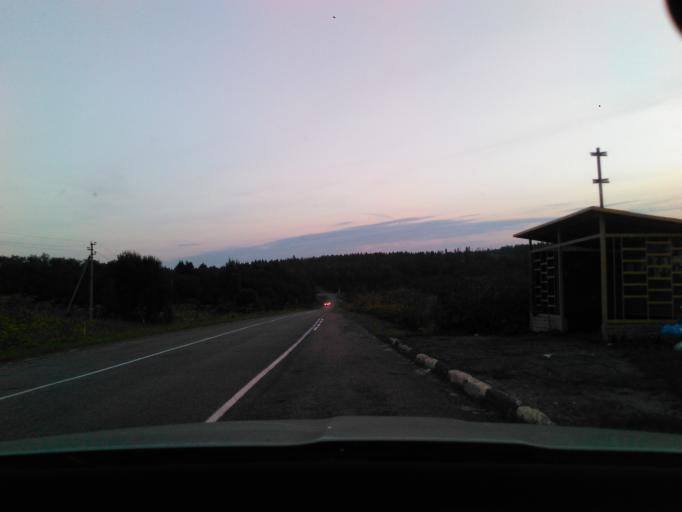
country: RU
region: Moskovskaya
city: Klin
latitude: 56.2138
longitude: 36.7249
